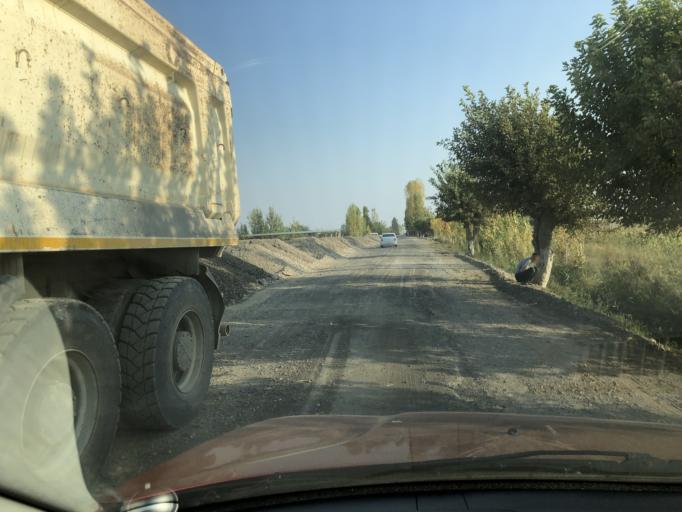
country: UZ
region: Namangan
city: Uychi
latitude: 41.0670
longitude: 71.9850
